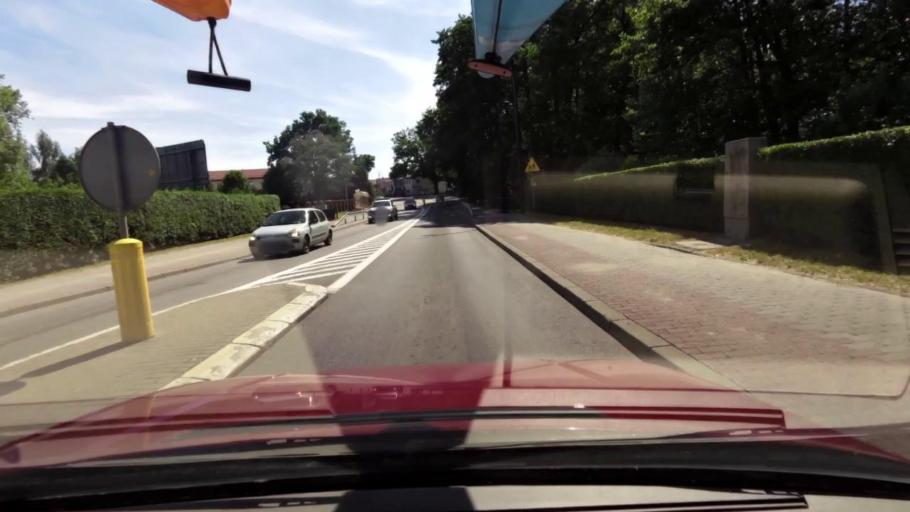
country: PL
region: Pomeranian Voivodeship
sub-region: Powiat slupski
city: Kobylnica
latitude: 54.4401
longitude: 16.9980
